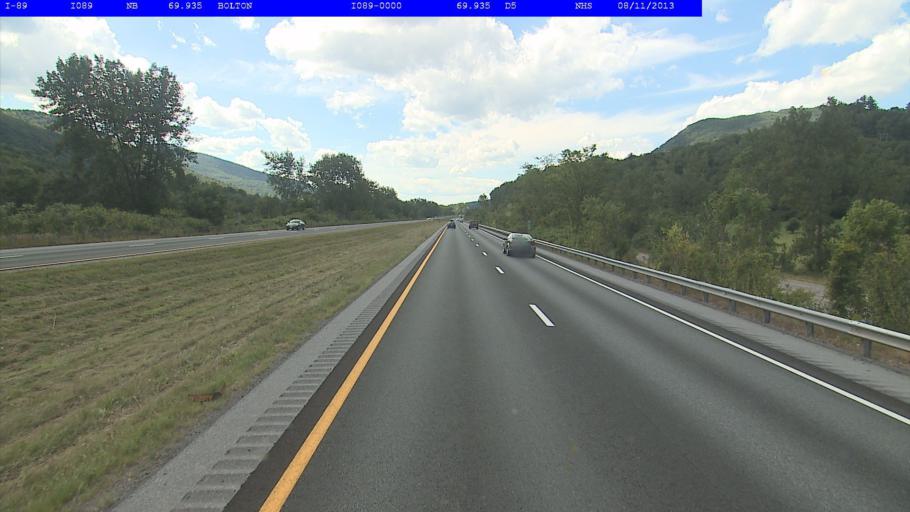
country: US
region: Vermont
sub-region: Washington County
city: Waterbury
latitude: 44.3696
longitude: -72.8670
